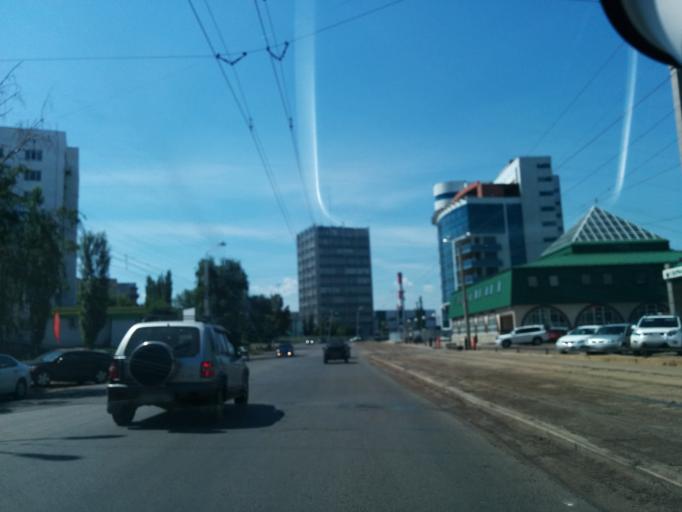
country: RU
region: Bashkortostan
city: Ufa
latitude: 54.7483
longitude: 55.9837
